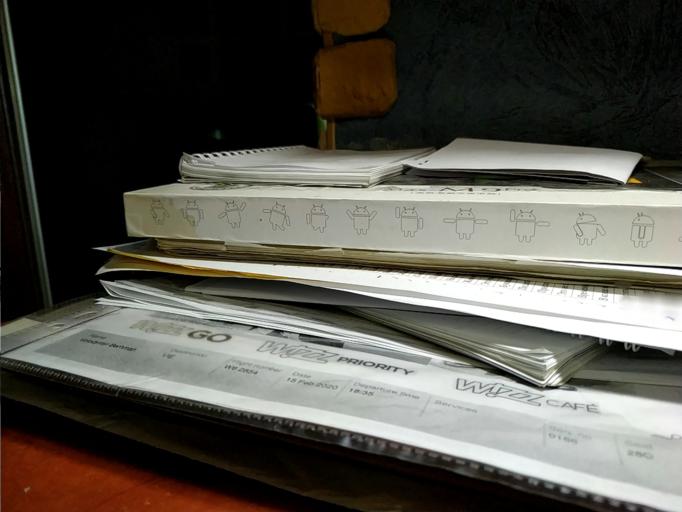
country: RU
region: Arkhangelskaya
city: Onega
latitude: 63.7785
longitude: 37.9817
